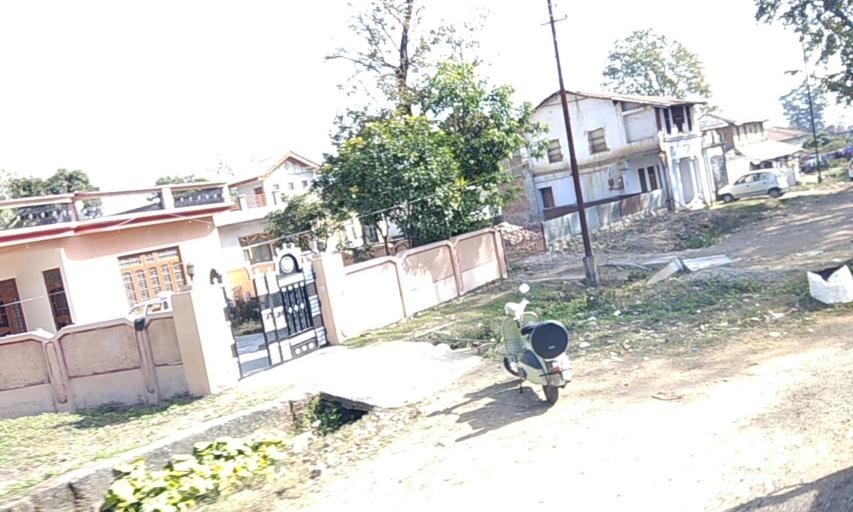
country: IN
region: Himachal Pradesh
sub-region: Kangra
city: Yol
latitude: 32.2185
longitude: 76.1777
